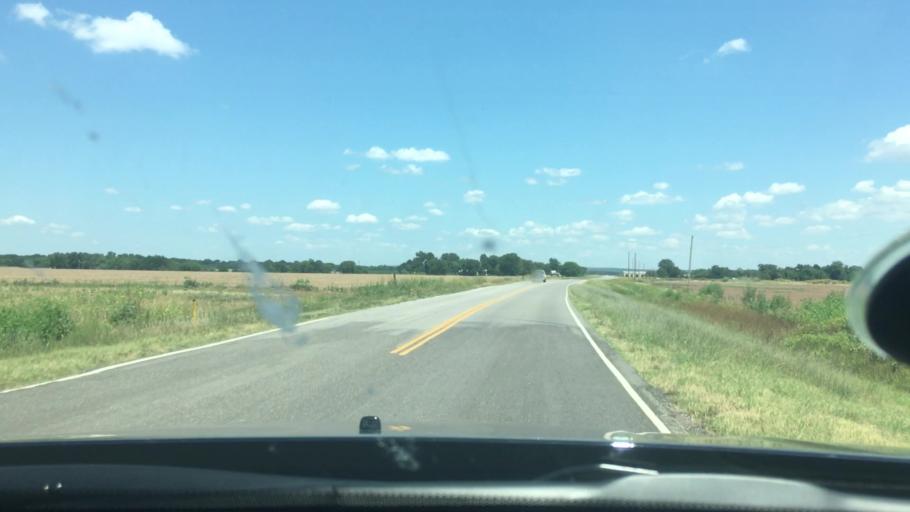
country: US
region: Oklahoma
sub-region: Carter County
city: Dickson
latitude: 34.2250
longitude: -96.9771
